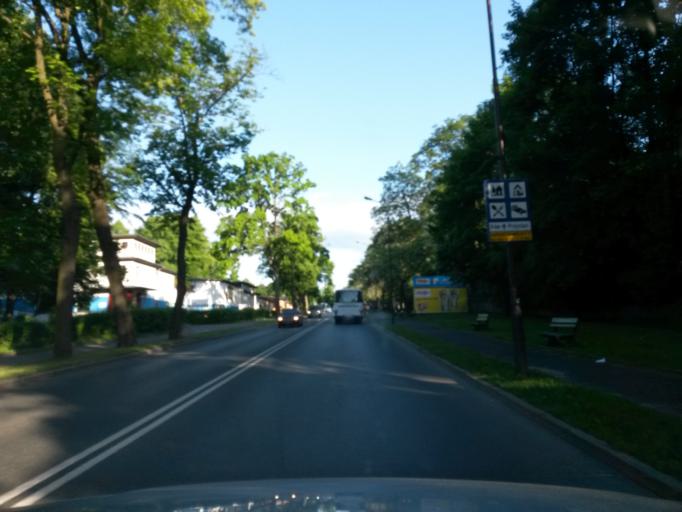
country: PL
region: Lower Silesian Voivodeship
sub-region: Jelenia Gora
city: Jelenia Gora
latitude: 50.8960
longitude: 15.7437
